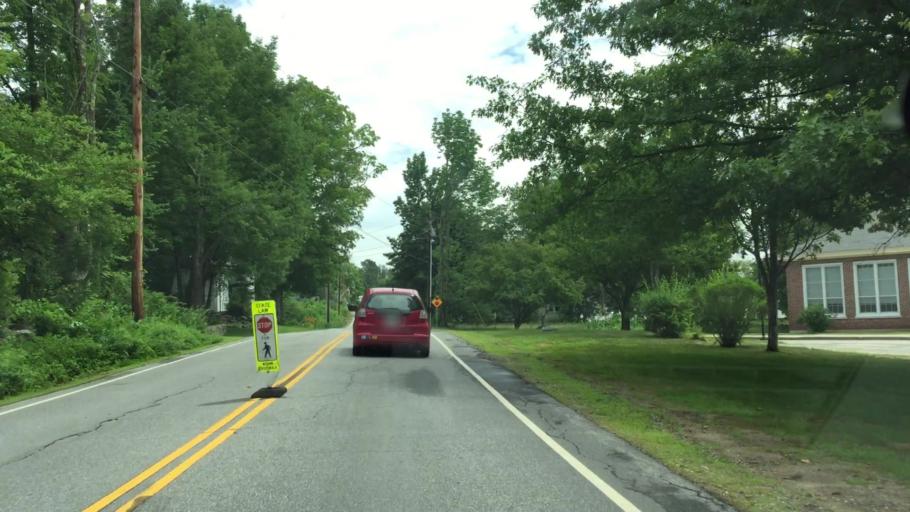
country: US
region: New Hampshire
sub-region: Carroll County
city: Sandwich
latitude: 43.8060
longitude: -71.4415
